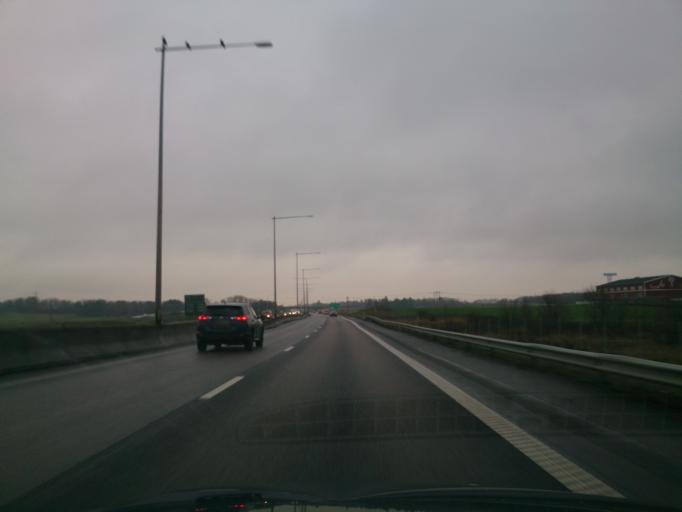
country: SE
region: OEstergoetland
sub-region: Norrkopings Kommun
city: Norrkoping
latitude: 58.5758
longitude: 16.0989
